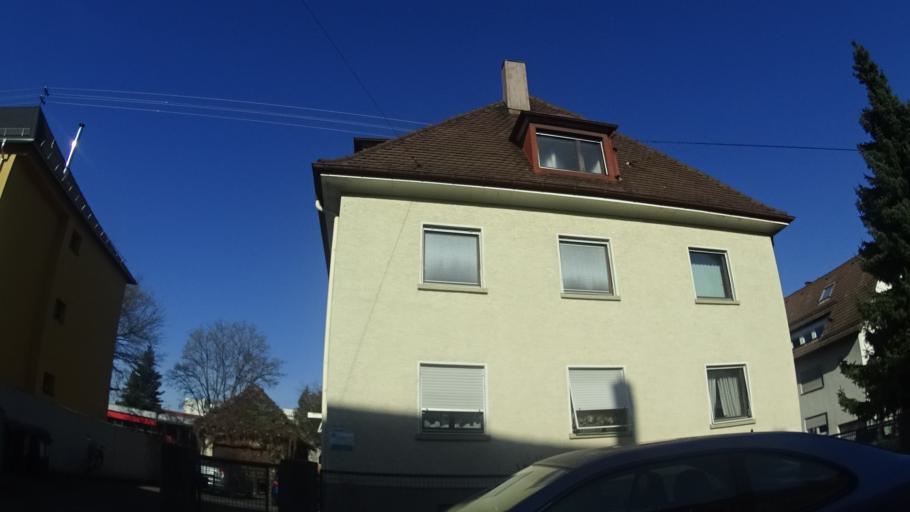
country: DE
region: Baden-Wuerttemberg
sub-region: Karlsruhe Region
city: Karlsruhe
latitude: 49.0144
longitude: 8.4464
